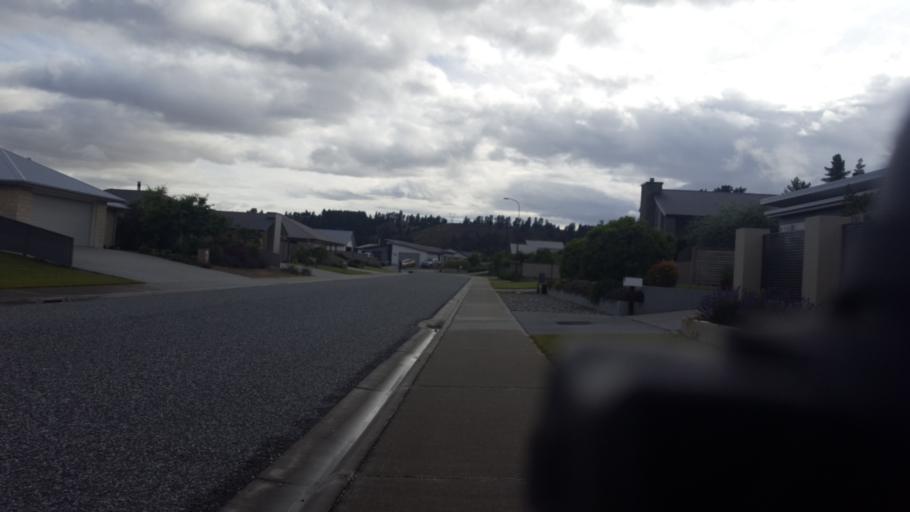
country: NZ
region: Otago
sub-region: Queenstown-Lakes District
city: Wanaka
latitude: -45.2408
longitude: 169.3810
